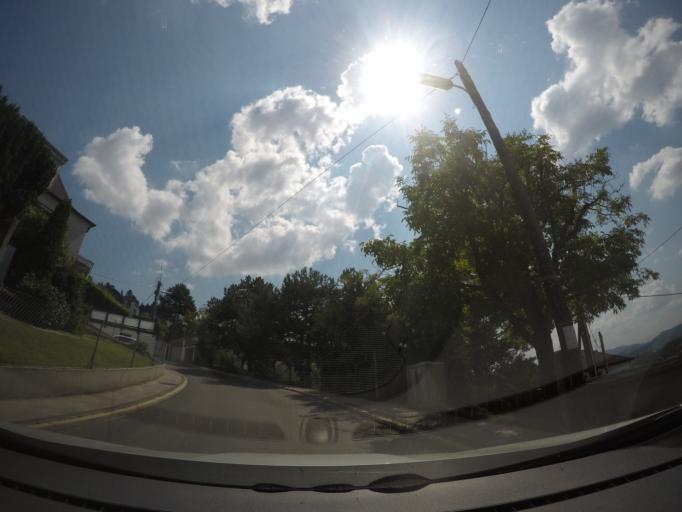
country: AT
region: Lower Austria
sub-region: Politischer Bezirk Wien-Umgebung
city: Purkersdorf
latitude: 48.2190
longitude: 16.2538
